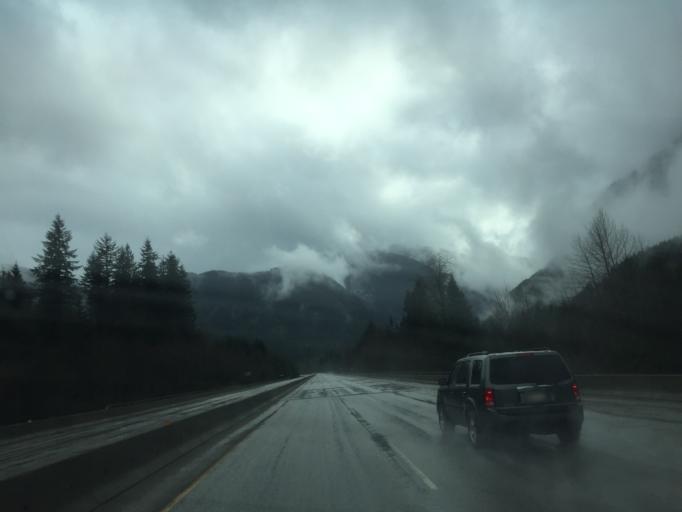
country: CA
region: British Columbia
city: Hope
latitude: 49.4771
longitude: -121.2536
